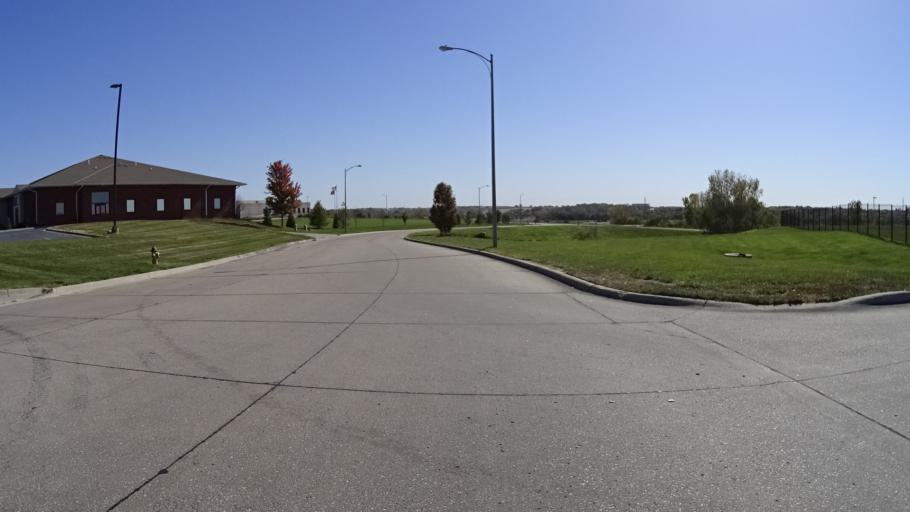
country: US
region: Nebraska
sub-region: Sarpy County
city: Papillion
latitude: 41.1610
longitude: -96.0276
